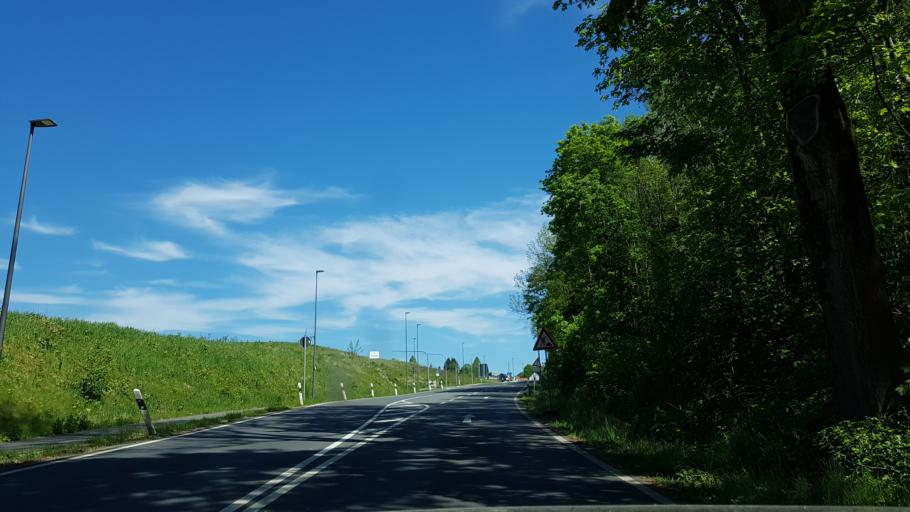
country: DE
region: North Rhine-Westphalia
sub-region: Regierungsbezirk Dusseldorf
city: Heiligenhaus
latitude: 51.3098
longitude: 6.9508
